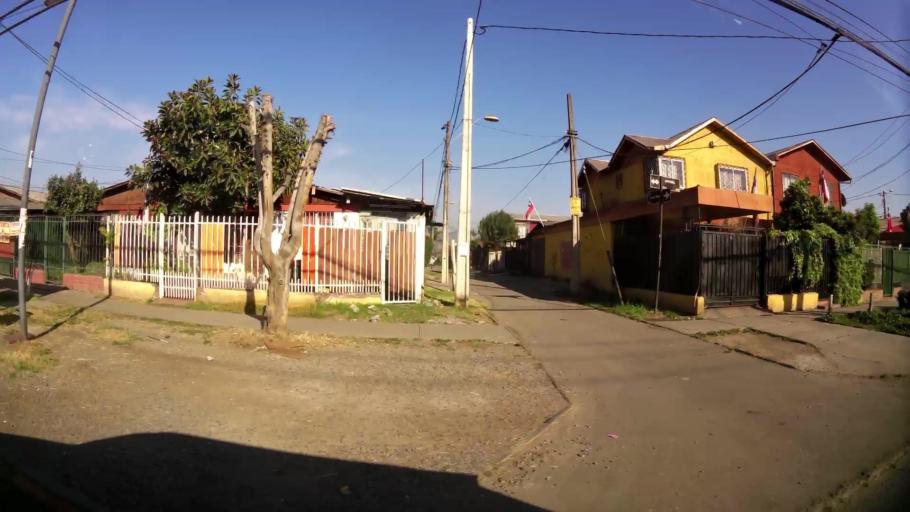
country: CL
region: Santiago Metropolitan
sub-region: Provincia de Santiago
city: Lo Prado
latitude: -33.4769
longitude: -70.7492
